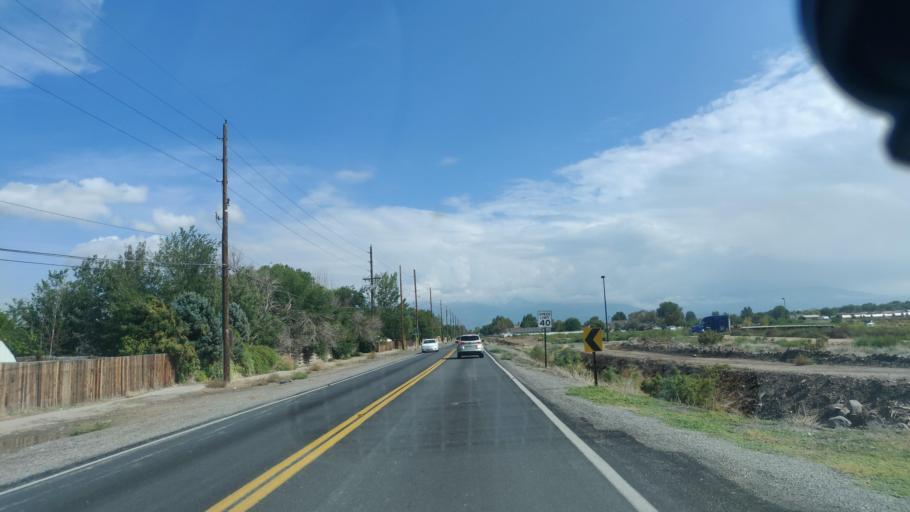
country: US
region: Colorado
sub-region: Mesa County
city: Orchard Mesa
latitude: 39.0412
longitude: -108.5381
